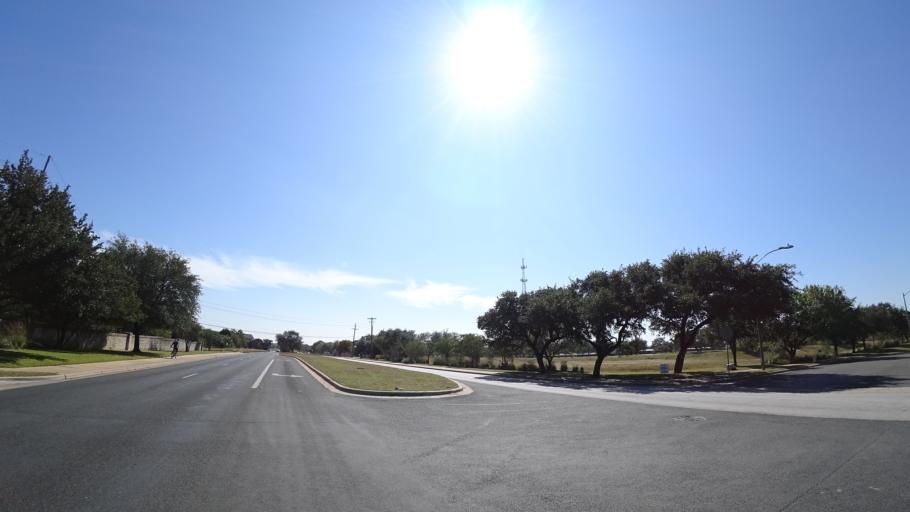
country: US
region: Texas
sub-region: Travis County
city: Shady Hollow
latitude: 30.1932
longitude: -97.8586
